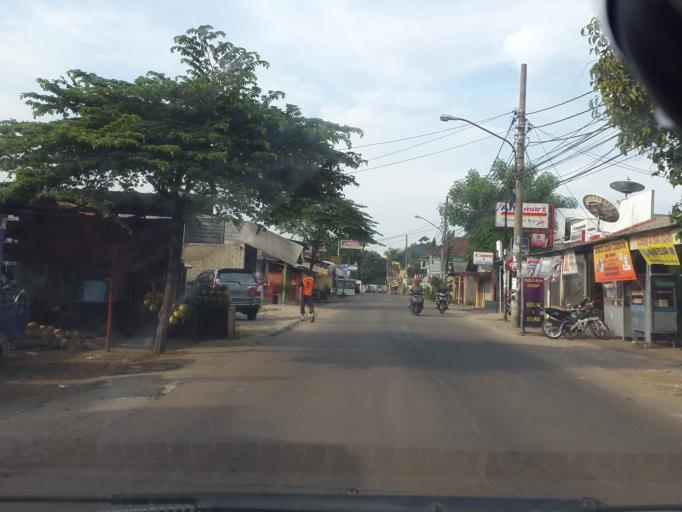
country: ID
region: Banten
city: South Tangerang
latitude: -6.2786
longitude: 106.6965
